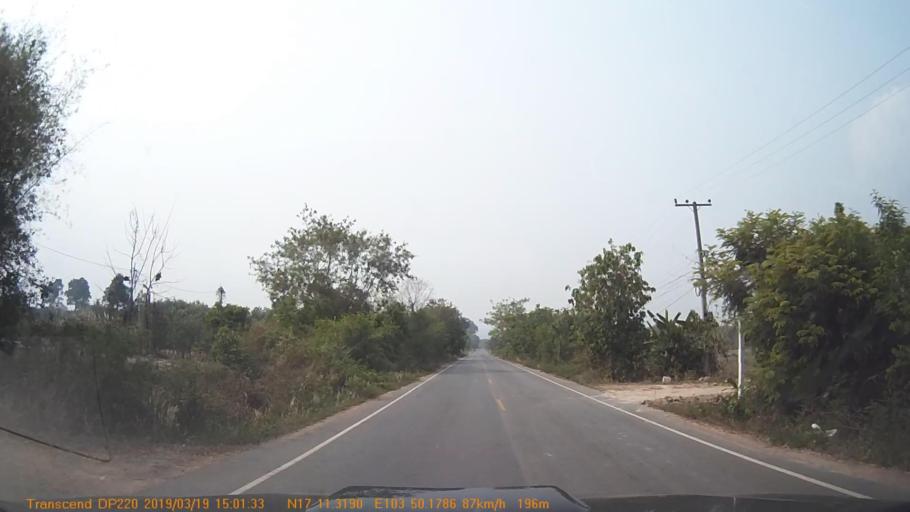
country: TH
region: Sakon Nakhon
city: Kut Bak
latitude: 17.1889
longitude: 103.8362
